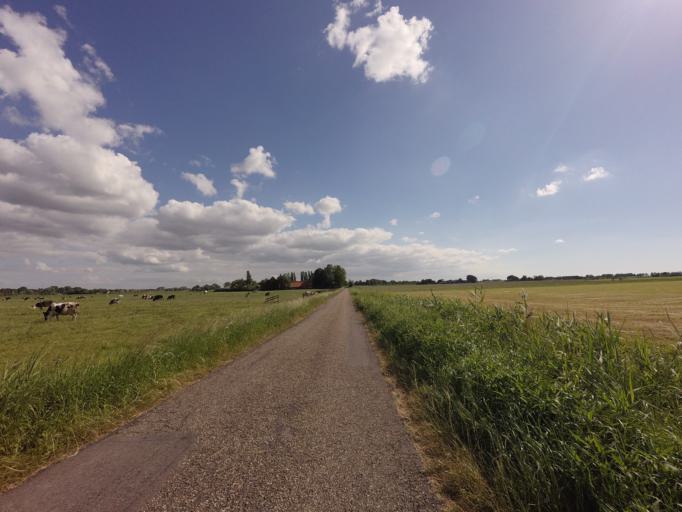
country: NL
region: Utrecht
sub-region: Gemeente De Ronde Venen
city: Mijdrecht
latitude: 52.2181
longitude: 4.8477
